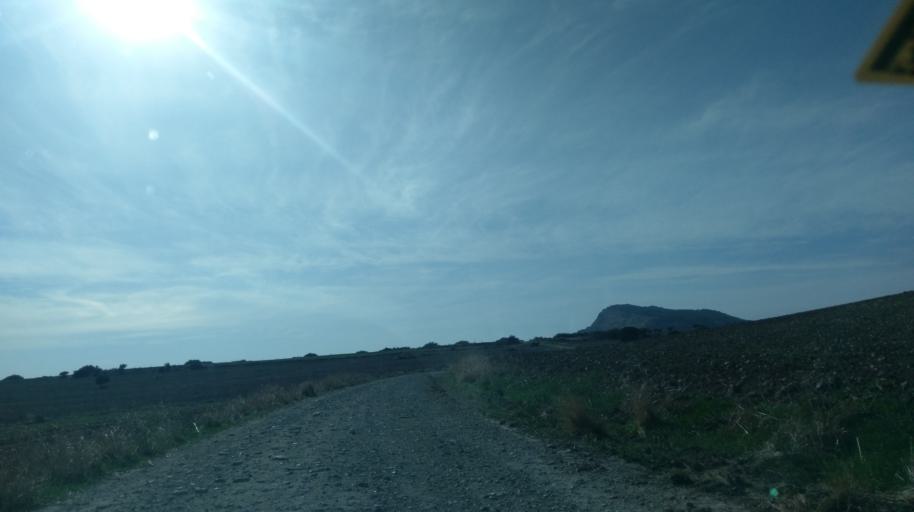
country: CY
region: Ammochostos
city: Trikomo
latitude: 35.3326
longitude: 33.8307
